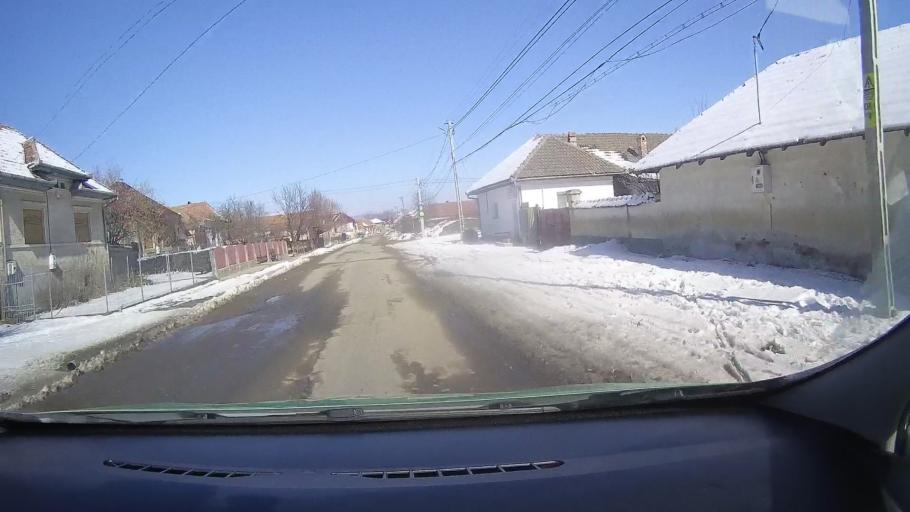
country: RO
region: Brasov
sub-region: Comuna Mandra
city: Mandra
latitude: 45.8202
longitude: 25.0053
